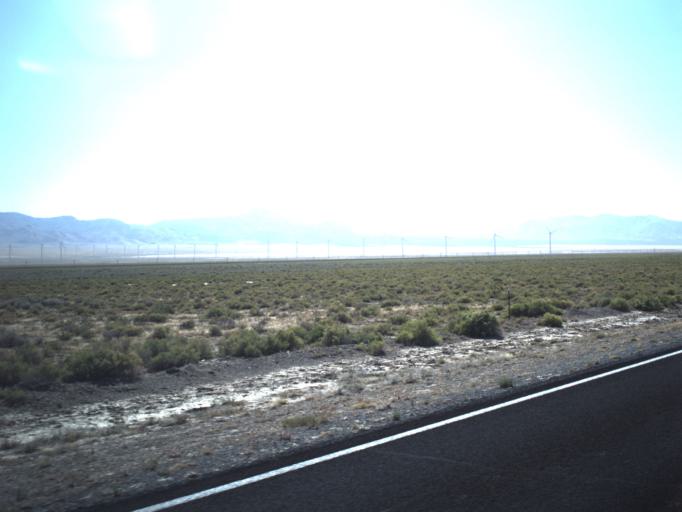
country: US
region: Utah
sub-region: Beaver County
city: Milford
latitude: 38.5364
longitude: -112.9912
